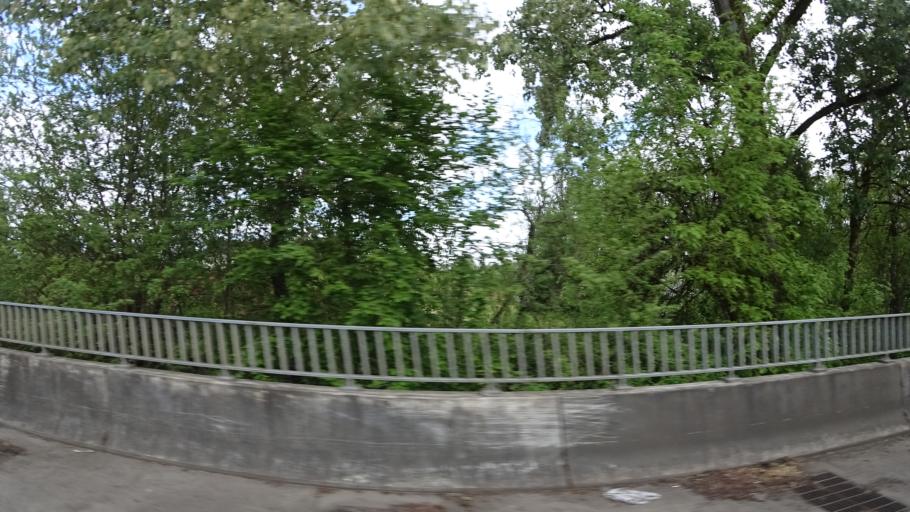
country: US
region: Oregon
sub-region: Washington County
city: Hillsboro
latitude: 45.4862
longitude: -122.9807
